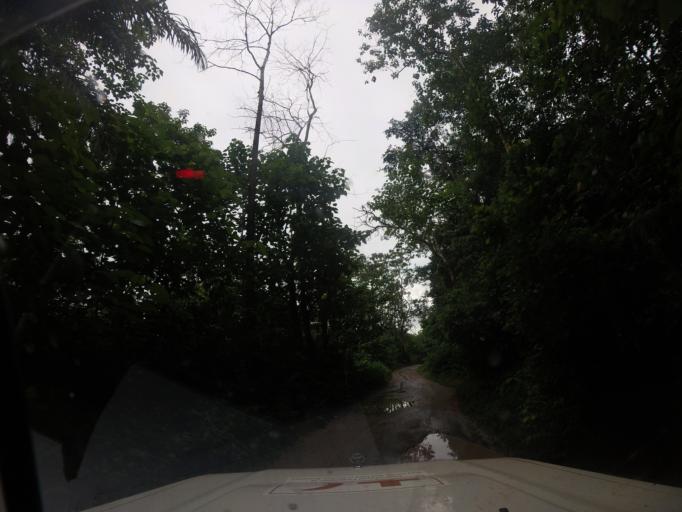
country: SL
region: Northern Province
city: Kamakwie
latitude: 9.5963
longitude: -12.2169
